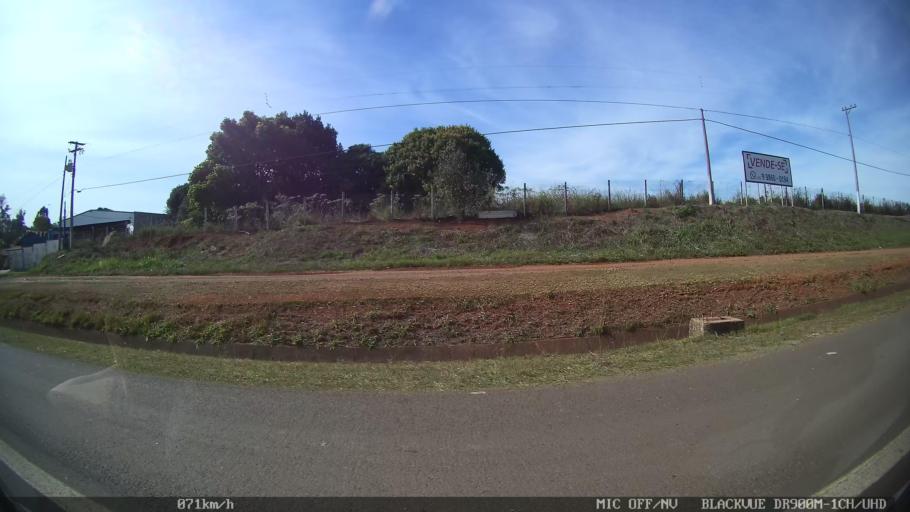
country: BR
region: Sao Paulo
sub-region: Piracicaba
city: Piracicaba
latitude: -22.7762
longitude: -47.6501
